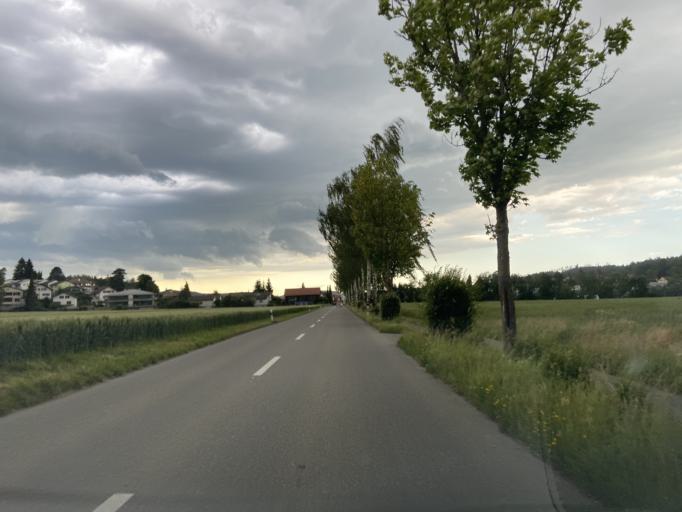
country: CH
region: Thurgau
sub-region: Muenchwilen District
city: Aadorf
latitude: 47.4808
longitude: 8.9052
